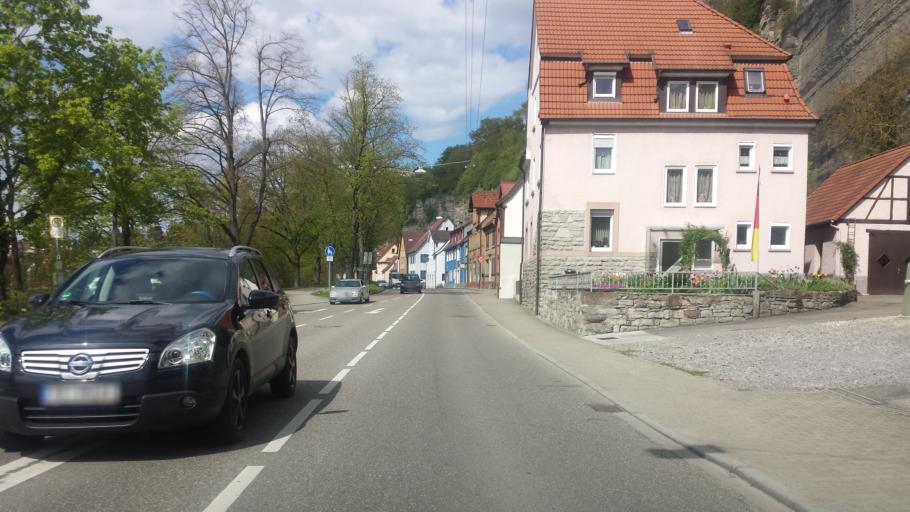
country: DE
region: Baden-Wuerttemberg
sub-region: Karlsruhe Region
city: Muhlacker
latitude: 48.9410
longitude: 8.8440
